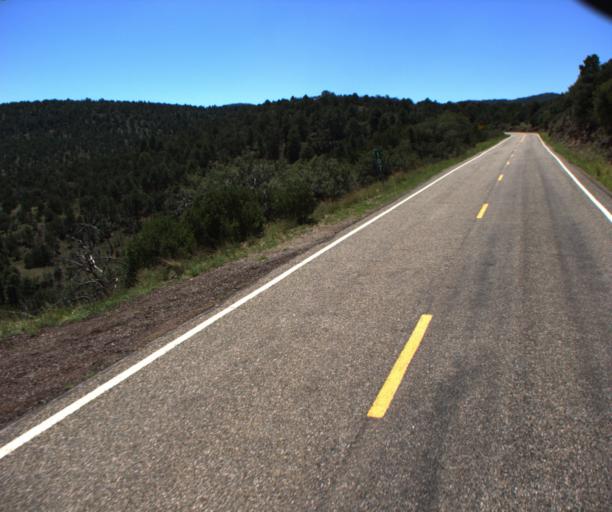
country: US
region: Arizona
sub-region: Greenlee County
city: Morenci
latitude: 33.2542
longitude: -109.3704
